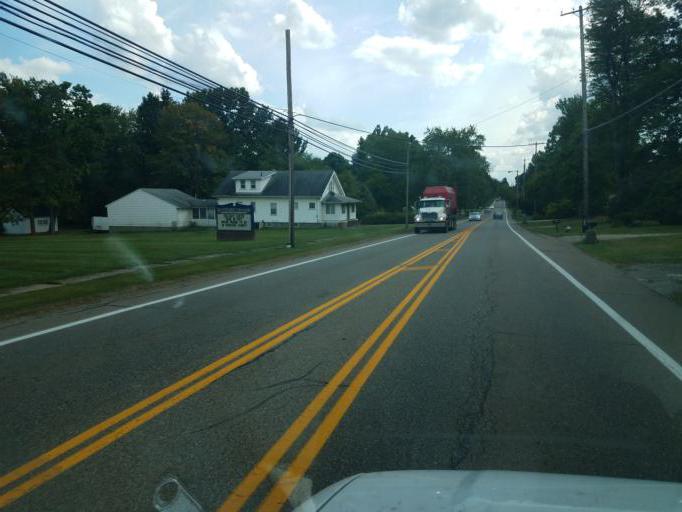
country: US
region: Ohio
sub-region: Portage County
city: Ravenna
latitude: 41.0982
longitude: -81.2426
